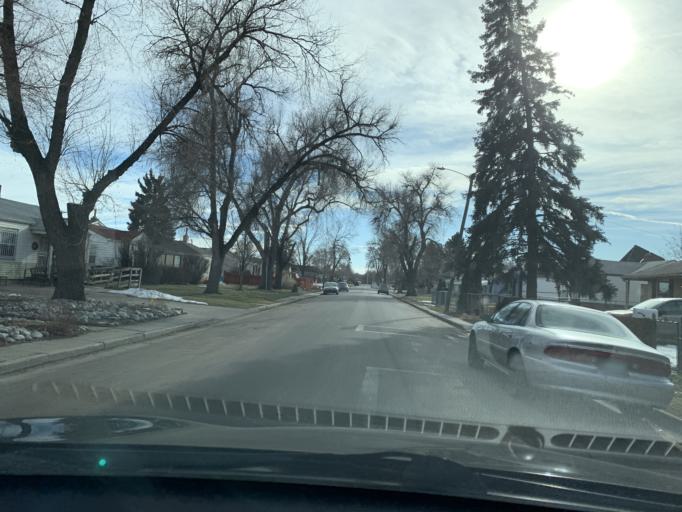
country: US
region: Colorado
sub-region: Denver County
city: Denver
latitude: 39.7324
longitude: -105.0264
